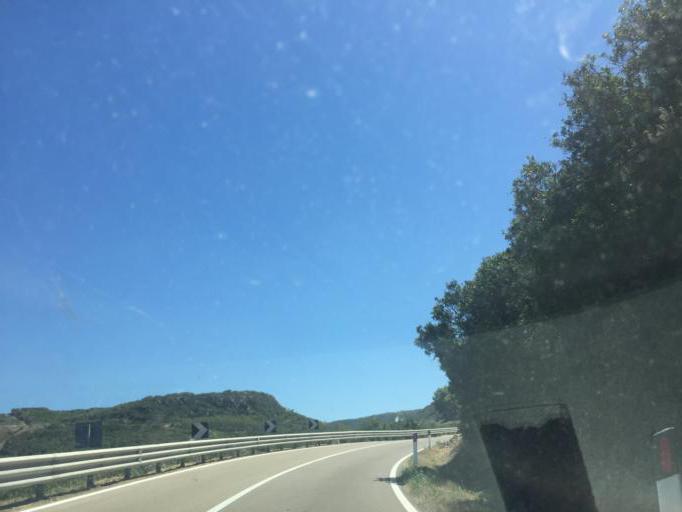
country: IT
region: Sardinia
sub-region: Provincia di Sassari
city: Castelsardo
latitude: 40.9094
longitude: 8.7375
